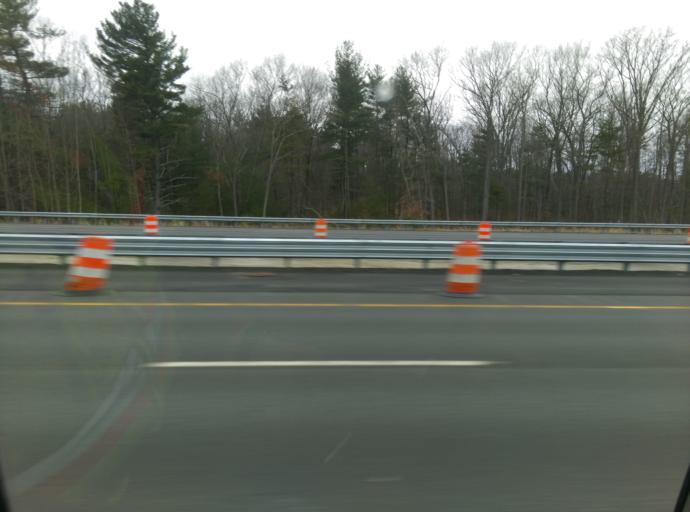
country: US
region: Massachusetts
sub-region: Essex County
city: Amesbury
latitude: 42.8497
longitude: -70.9000
